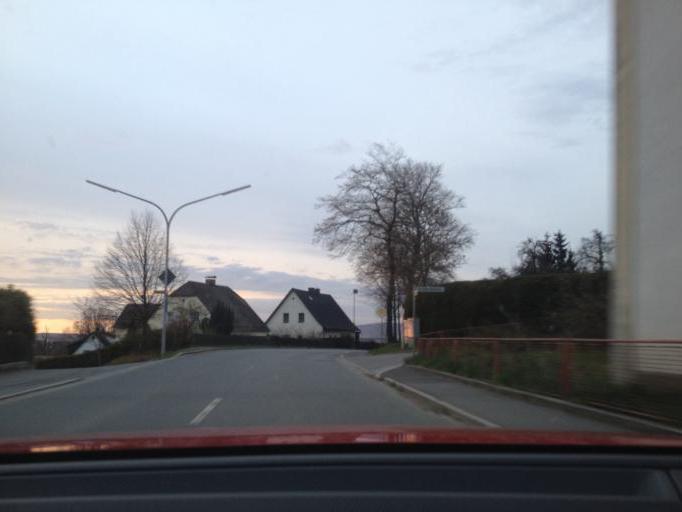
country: DE
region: Bavaria
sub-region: Upper Palatinate
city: Speinshart
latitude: 49.8273
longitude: 11.8388
